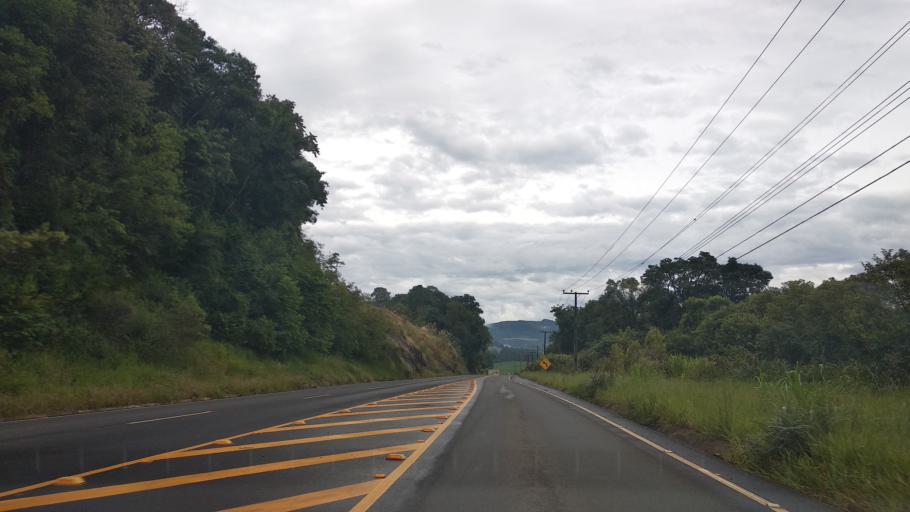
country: BR
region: Santa Catarina
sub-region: Videira
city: Videira
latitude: -27.0631
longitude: -51.2330
